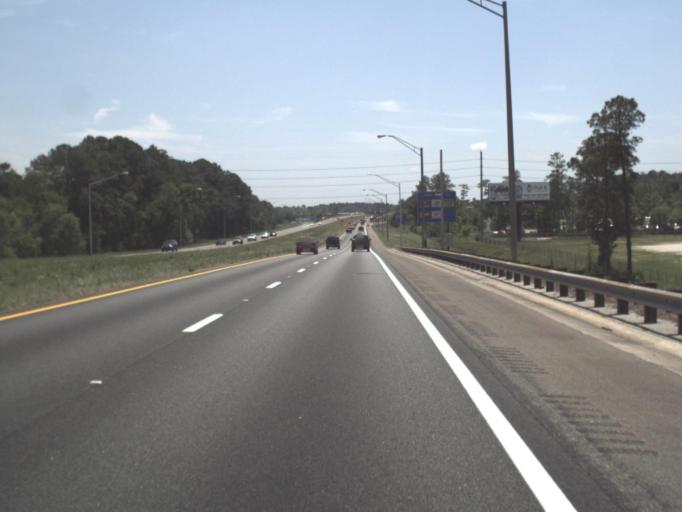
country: US
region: Florida
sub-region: Duval County
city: Jacksonville
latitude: 30.3454
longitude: -81.7610
